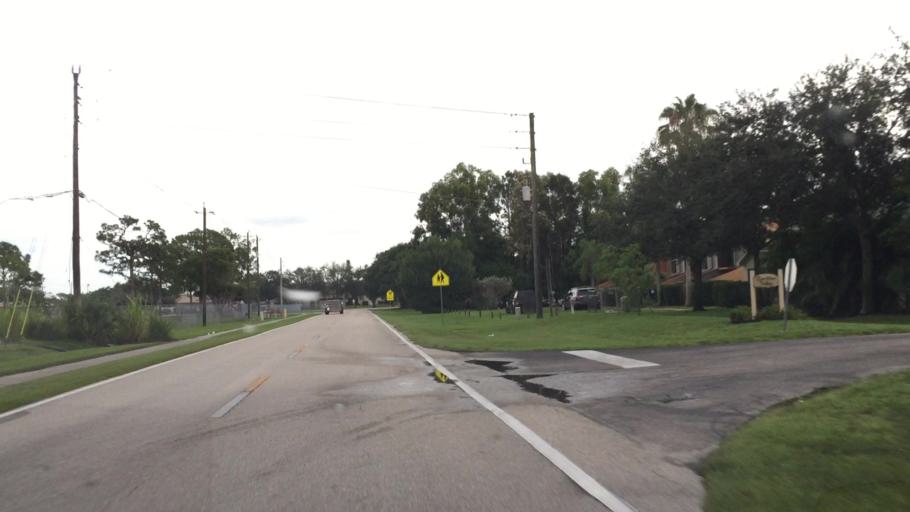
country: US
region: Florida
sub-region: Lee County
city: Pine Manor
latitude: 26.5677
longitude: -81.8702
